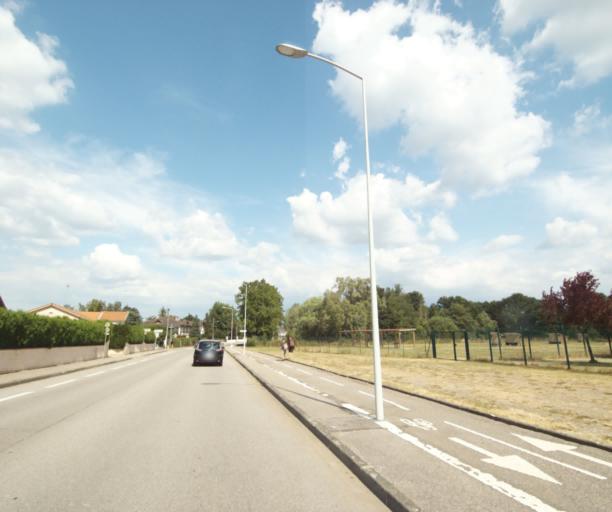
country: FR
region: Lorraine
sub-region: Departement de Meurthe-et-Moselle
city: Luneville
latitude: 48.5981
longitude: 6.5140
